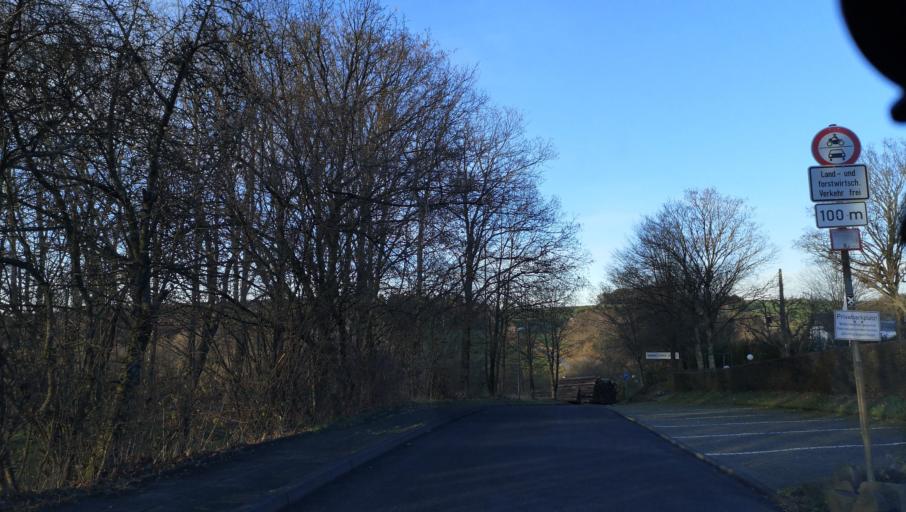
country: DE
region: North Rhine-Westphalia
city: Radevormwald
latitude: 51.2109
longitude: 7.3503
